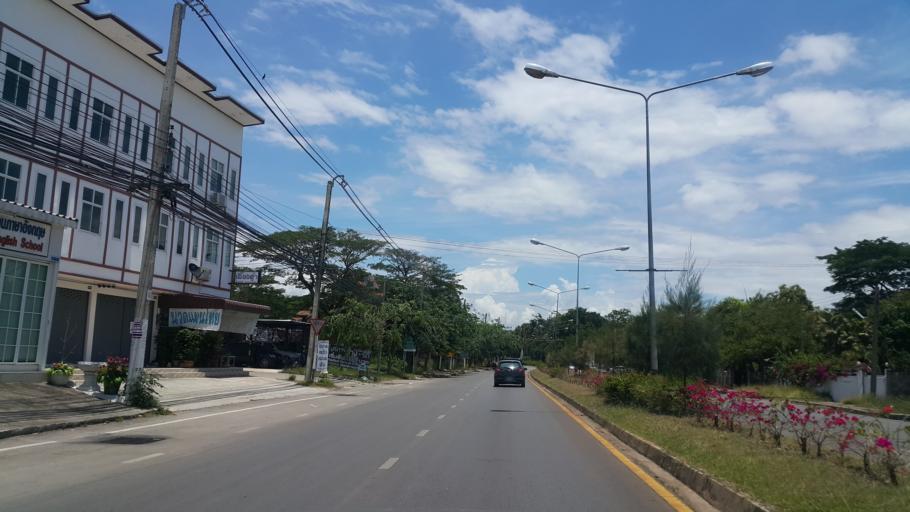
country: TH
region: Phayao
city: Phayao
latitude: 19.1793
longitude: 99.8864
